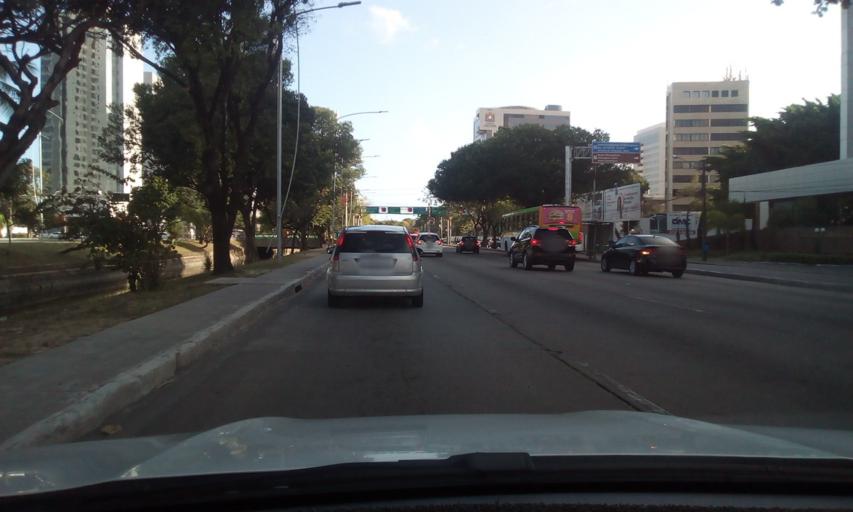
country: BR
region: Pernambuco
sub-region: Recife
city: Recife
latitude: -8.0611
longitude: -34.8978
